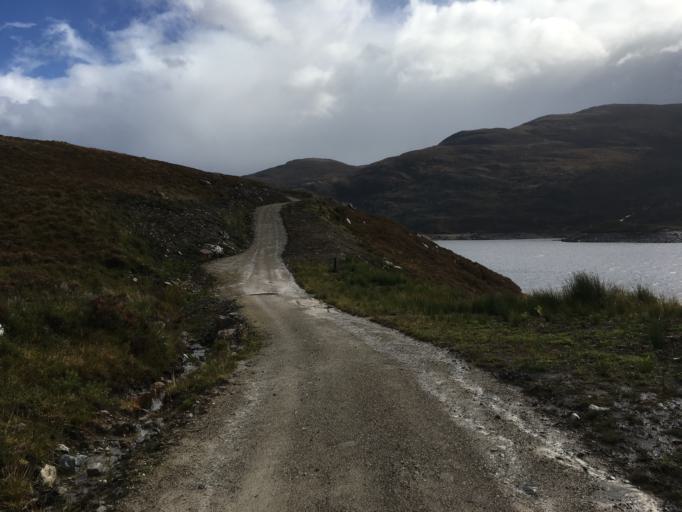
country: GB
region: Scotland
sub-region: Highland
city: Spean Bridge
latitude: 57.3407
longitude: -4.9731
